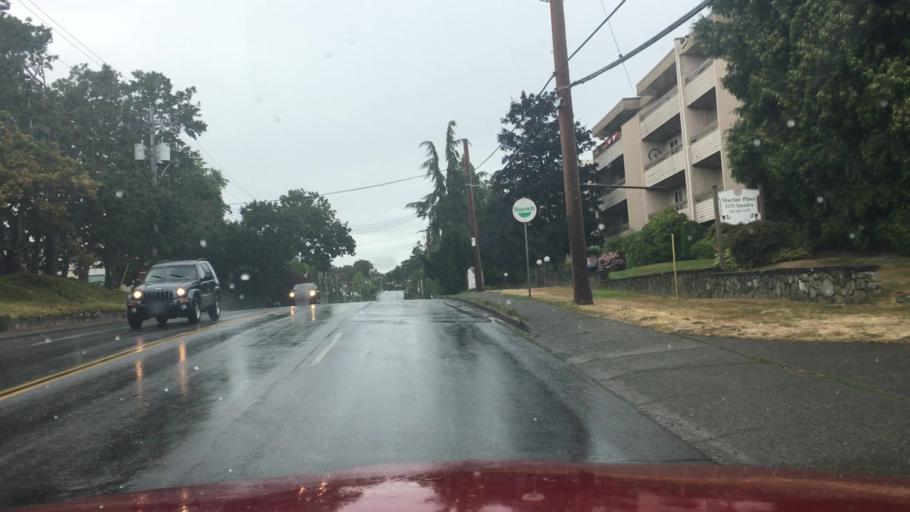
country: CA
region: British Columbia
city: Victoria
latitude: 48.4498
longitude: -123.3615
